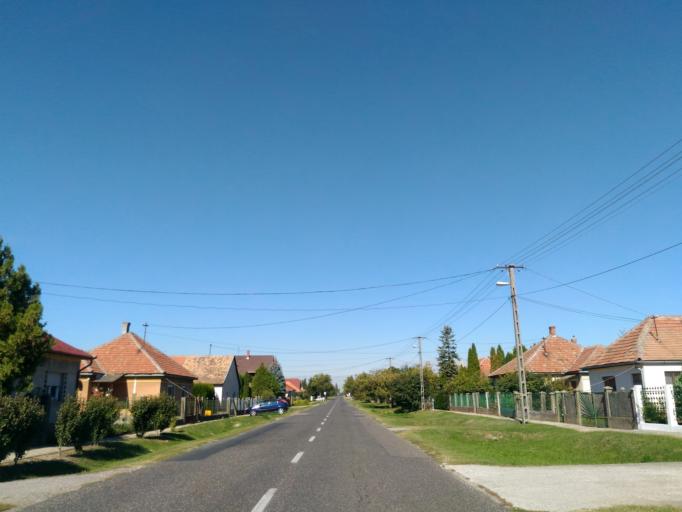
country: HU
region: Fejer
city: Ivancsa
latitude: 47.1653
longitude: 18.8223
